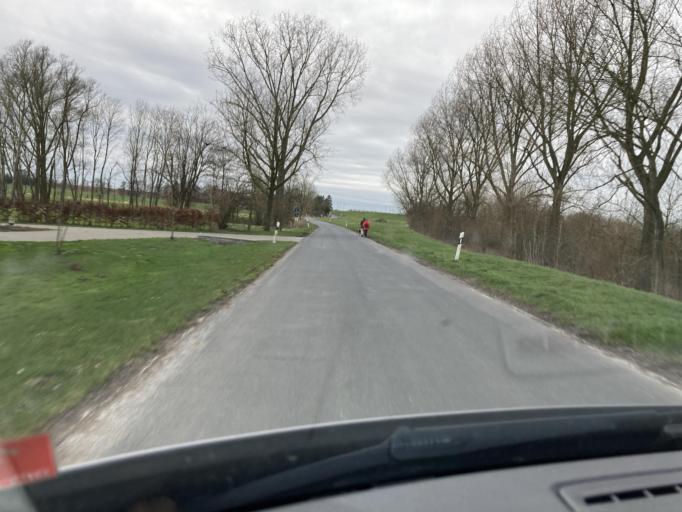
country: DE
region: Lower Saxony
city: Leer
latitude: 53.2100
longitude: 7.4735
